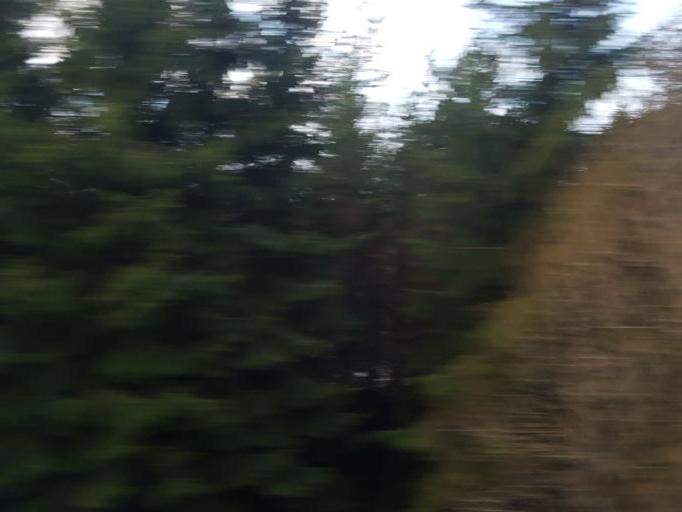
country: NO
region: Sor-Trondelag
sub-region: Melhus
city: Lundamo
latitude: 63.2181
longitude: 10.2939
